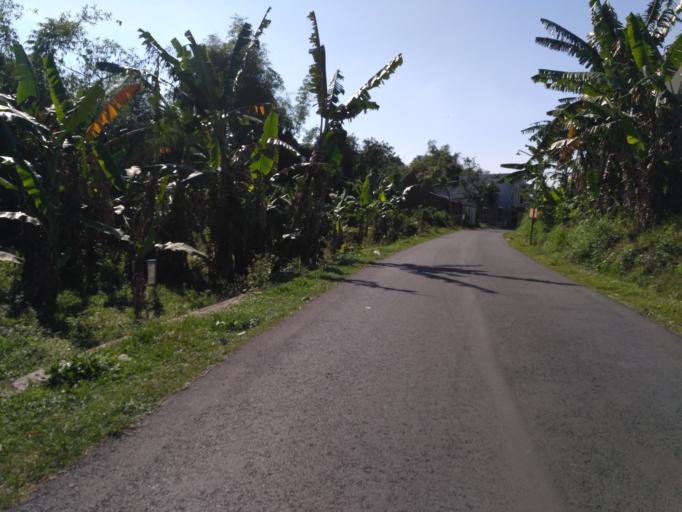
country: ID
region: East Java
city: Singosari
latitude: -7.9301
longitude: 112.6652
